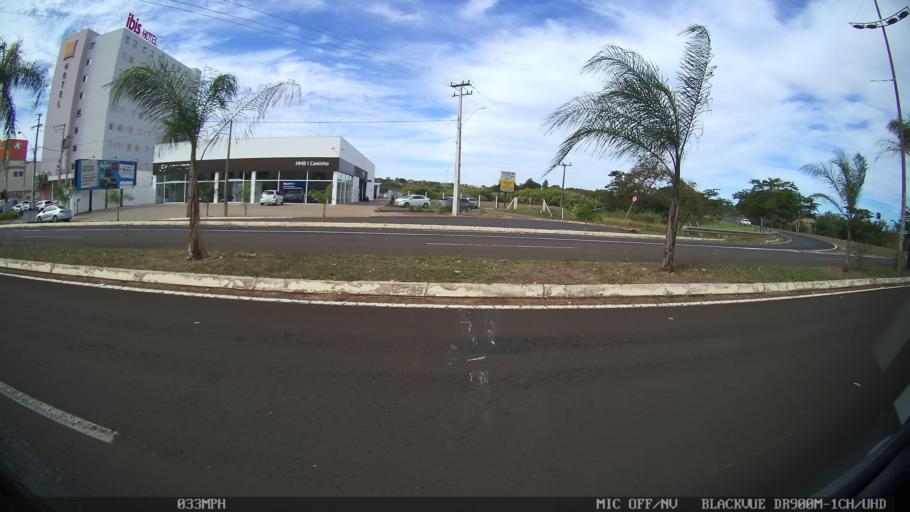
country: BR
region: Sao Paulo
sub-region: Catanduva
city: Catanduva
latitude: -21.1589
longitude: -48.9857
